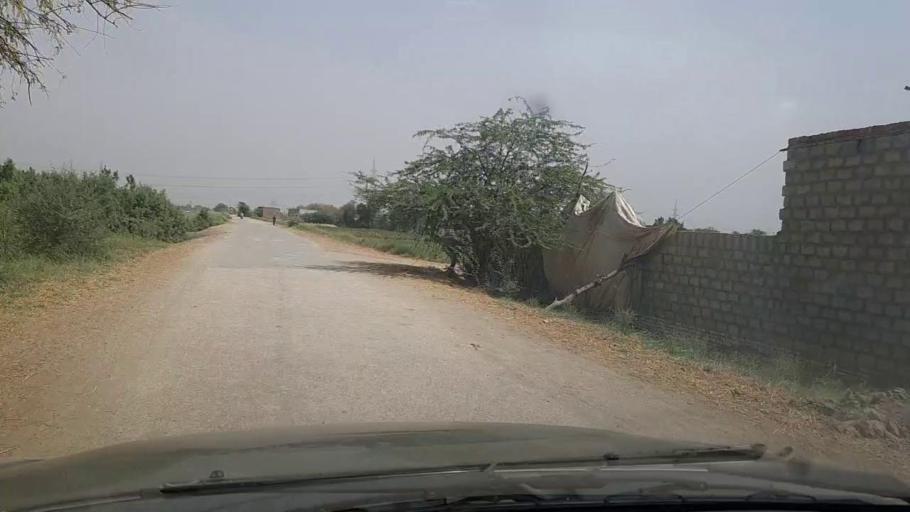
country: PK
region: Sindh
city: Shikarpur
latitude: 27.9251
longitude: 68.6682
